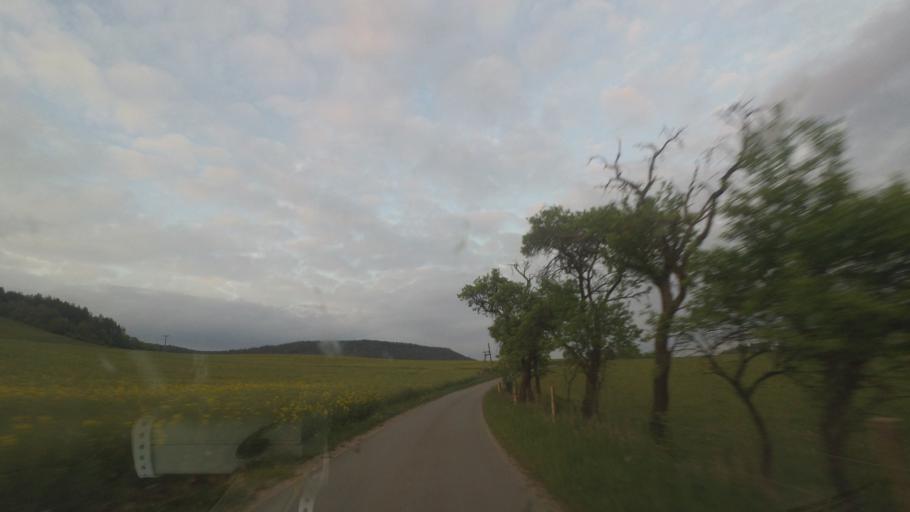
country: DE
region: Thuringia
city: Rottenbach
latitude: 50.7144
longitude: 11.1498
